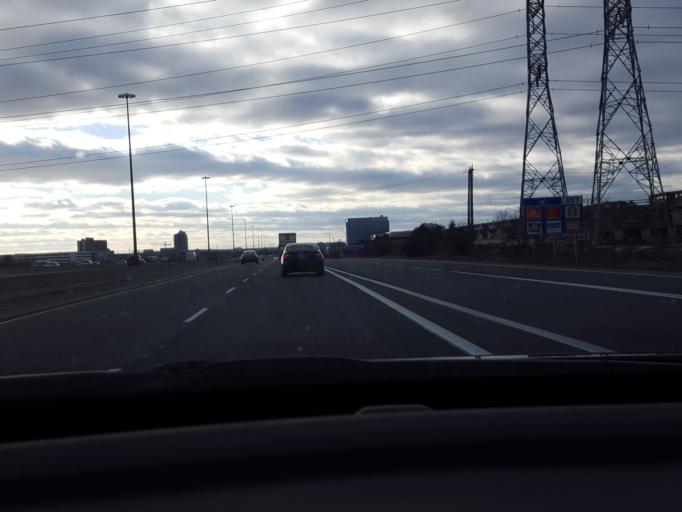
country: CA
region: Ontario
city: Ajax
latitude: 43.8375
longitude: -79.0745
